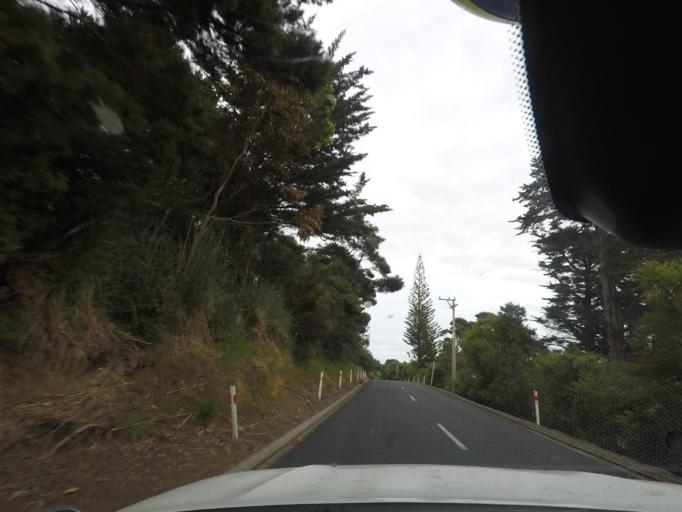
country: NZ
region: Auckland
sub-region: Auckland
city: Parakai
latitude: -36.5191
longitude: 174.2631
